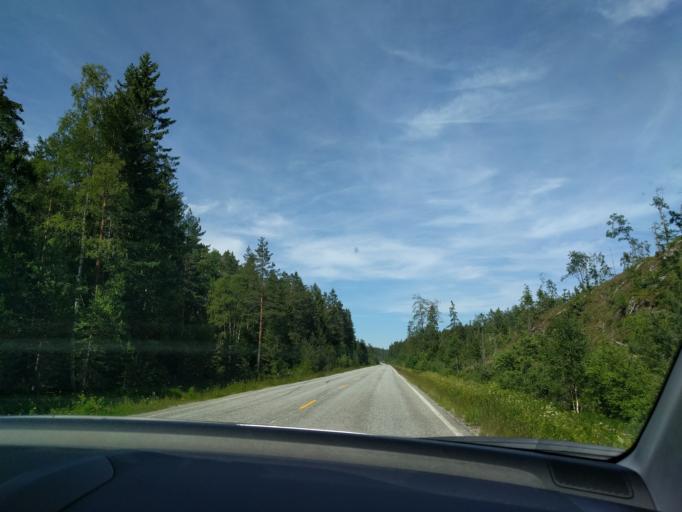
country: NO
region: Aust-Agder
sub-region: Gjerstad
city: Gjerstad
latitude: 58.8630
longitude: 9.1456
